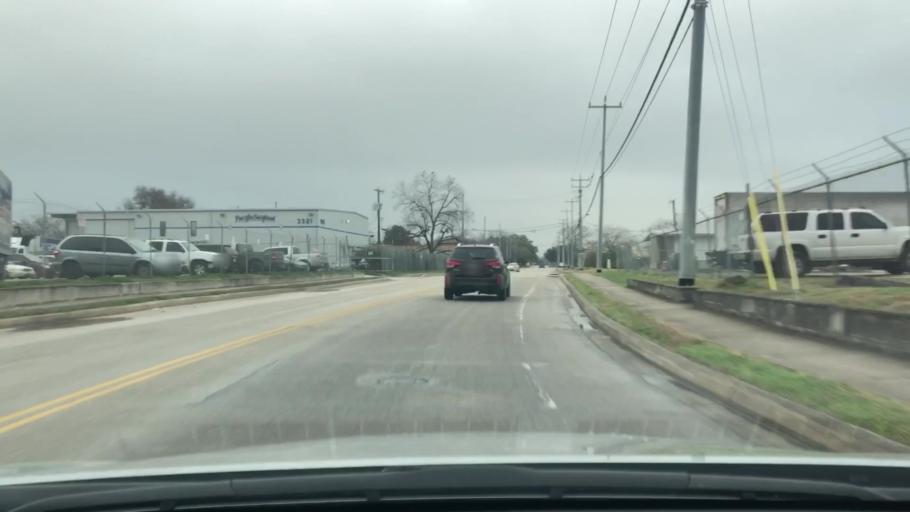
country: US
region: Texas
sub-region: Bexar County
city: Terrell Hills
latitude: 29.4394
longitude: -98.4341
